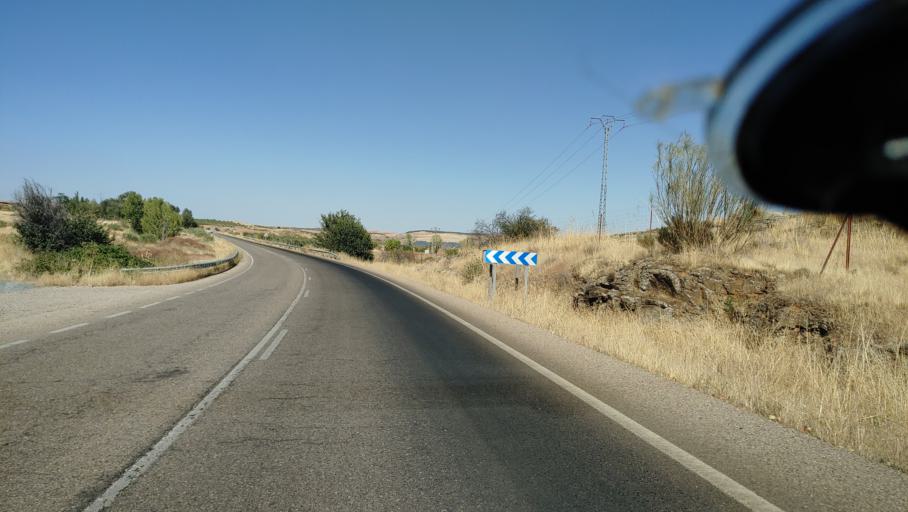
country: ES
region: Castille-La Mancha
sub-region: Province of Toledo
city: Casasbuenas
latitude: 39.7279
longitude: -4.1119
